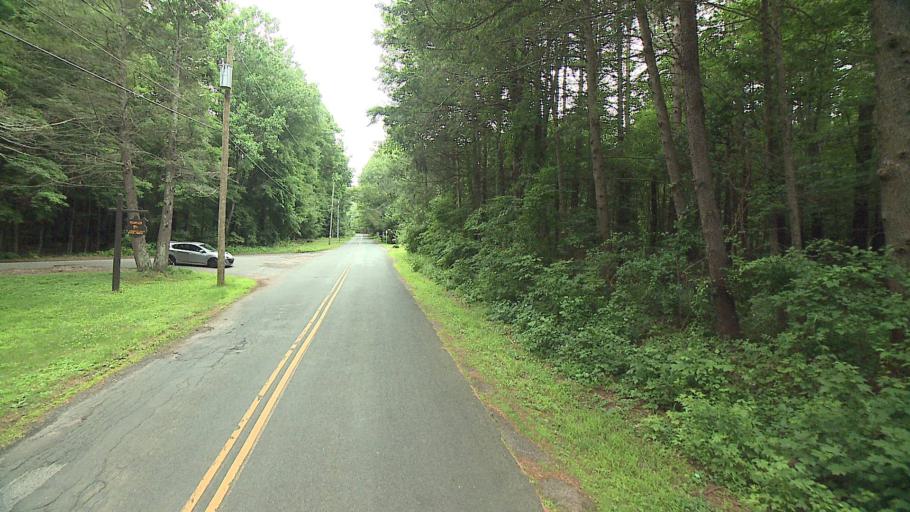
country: US
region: Connecticut
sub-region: Litchfield County
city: New Hartford Center
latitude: 41.9230
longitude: -72.9959
